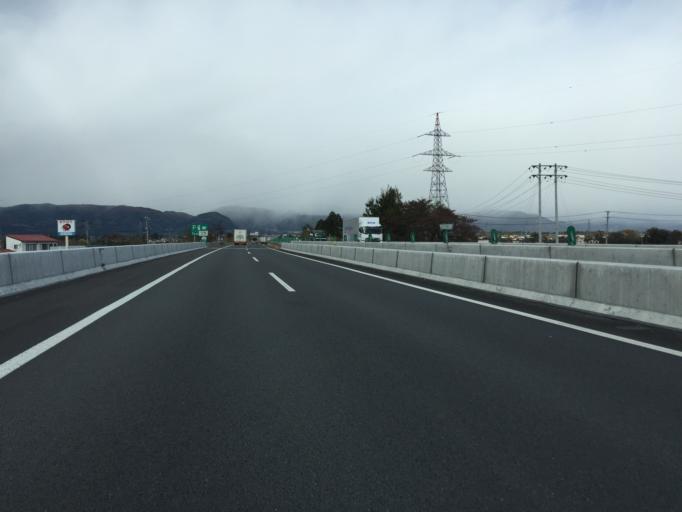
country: JP
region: Fukushima
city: Fukushima-shi
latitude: 37.7489
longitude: 140.4114
